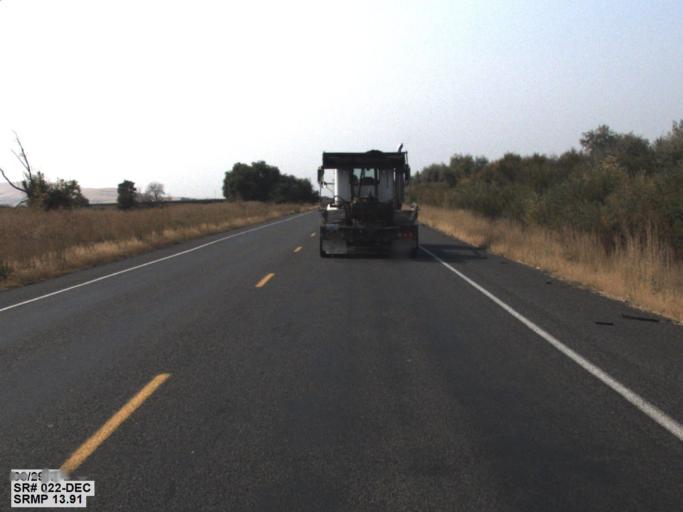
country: US
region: Washington
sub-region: Yakima County
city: Granger
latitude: 46.2786
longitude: -120.1624
